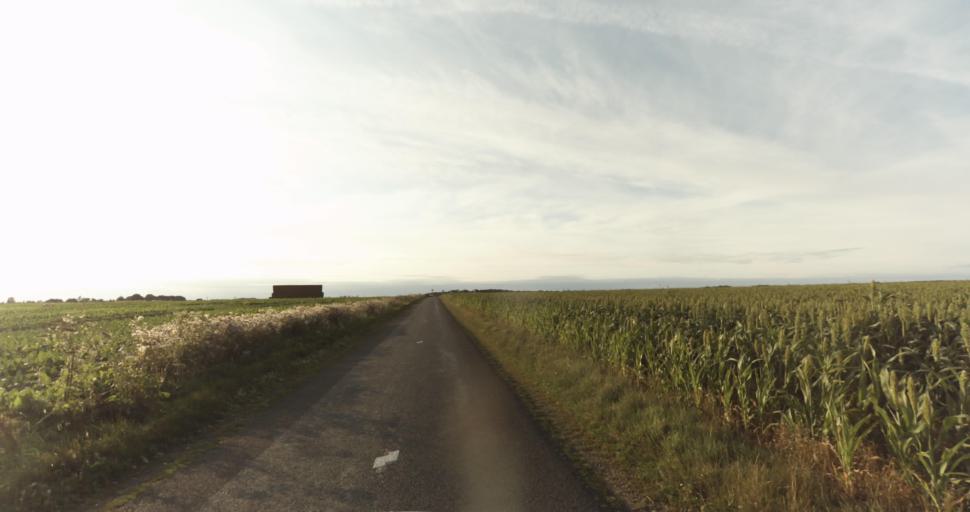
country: FR
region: Haute-Normandie
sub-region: Departement de l'Eure
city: Marcilly-sur-Eure
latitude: 48.8189
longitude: 1.2917
